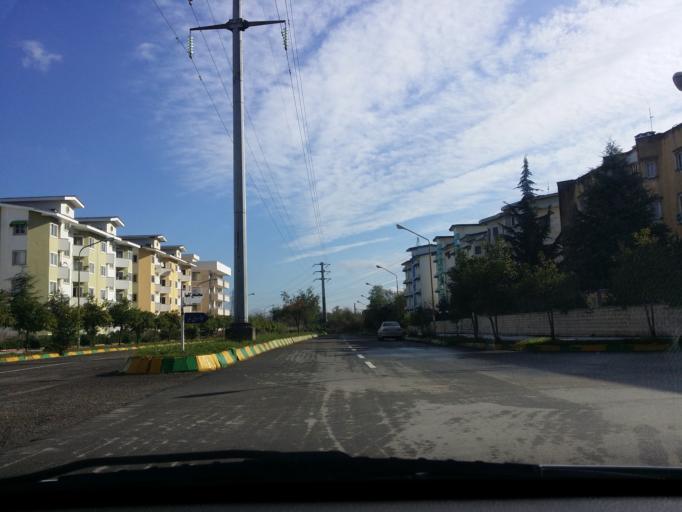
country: IR
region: Mazandaran
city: Chalus
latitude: 36.6744
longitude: 51.3120
